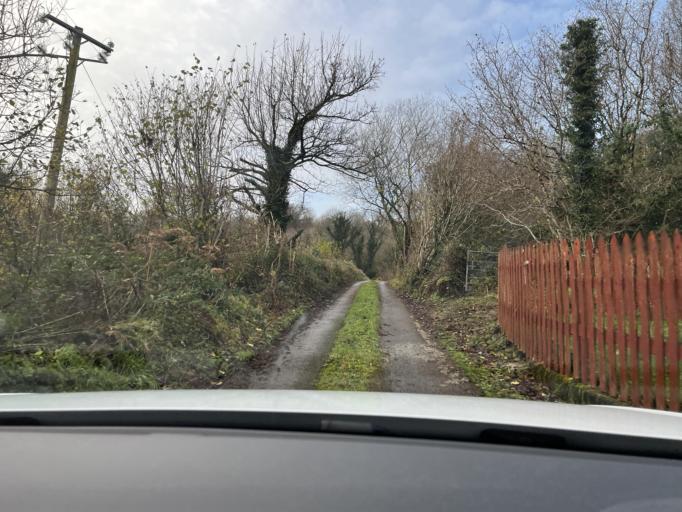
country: IE
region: Connaught
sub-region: Sligo
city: Sligo
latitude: 54.2678
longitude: -8.3498
